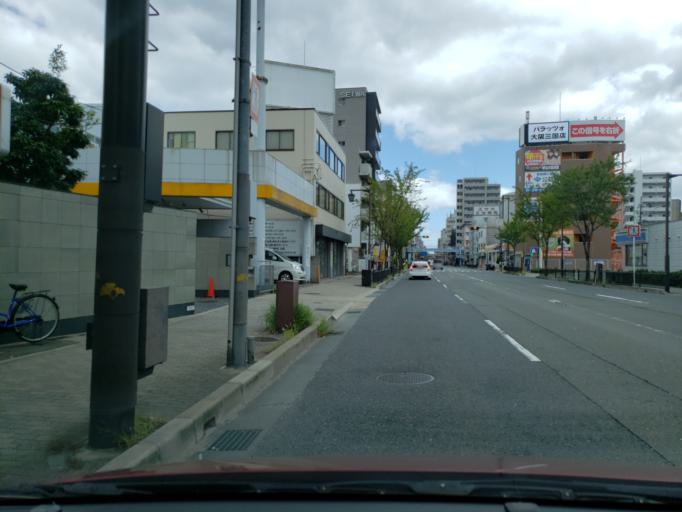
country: JP
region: Osaka
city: Suita
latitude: 34.7577
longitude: 135.4907
